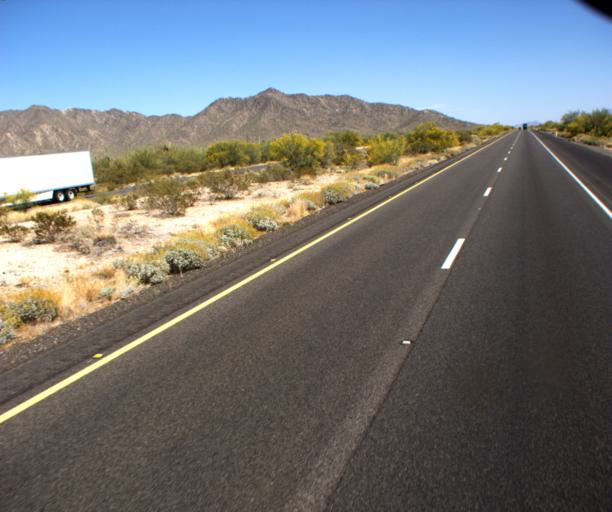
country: US
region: Arizona
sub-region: Maricopa County
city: Gila Bend
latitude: 32.8698
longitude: -112.4317
